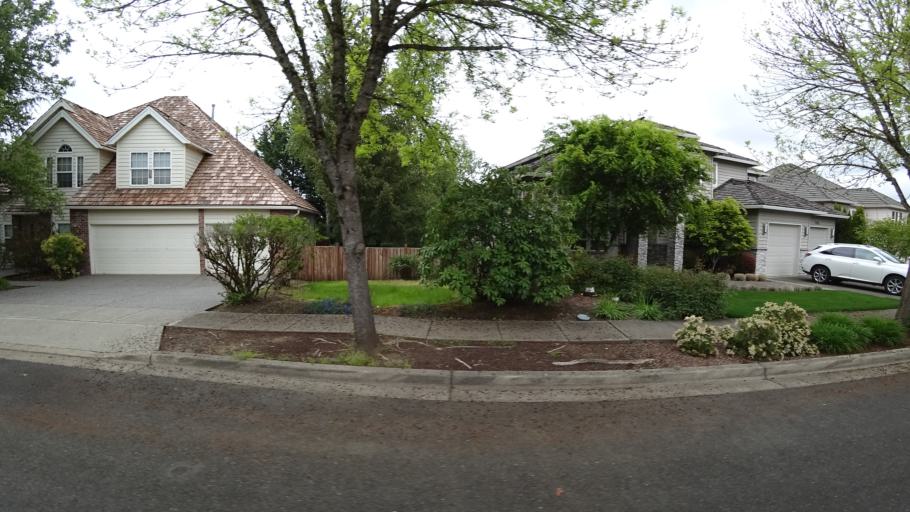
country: US
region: Oregon
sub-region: Washington County
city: Beaverton
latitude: 45.4588
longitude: -122.8294
